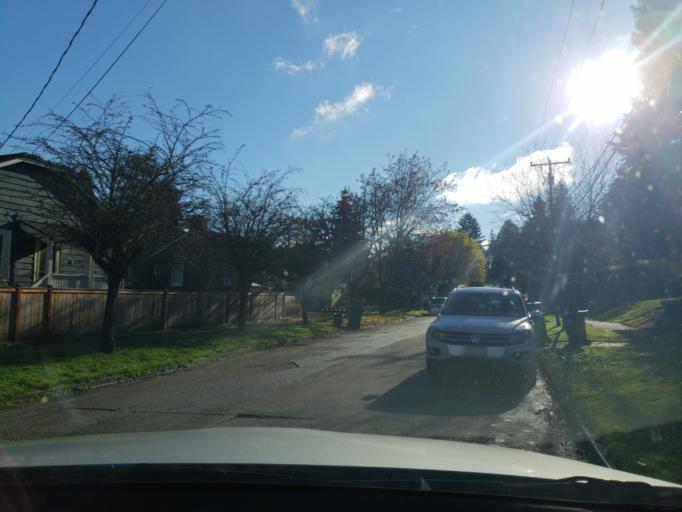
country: US
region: Washington
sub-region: King County
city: Seattle
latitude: 47.6777
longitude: -122.3500
